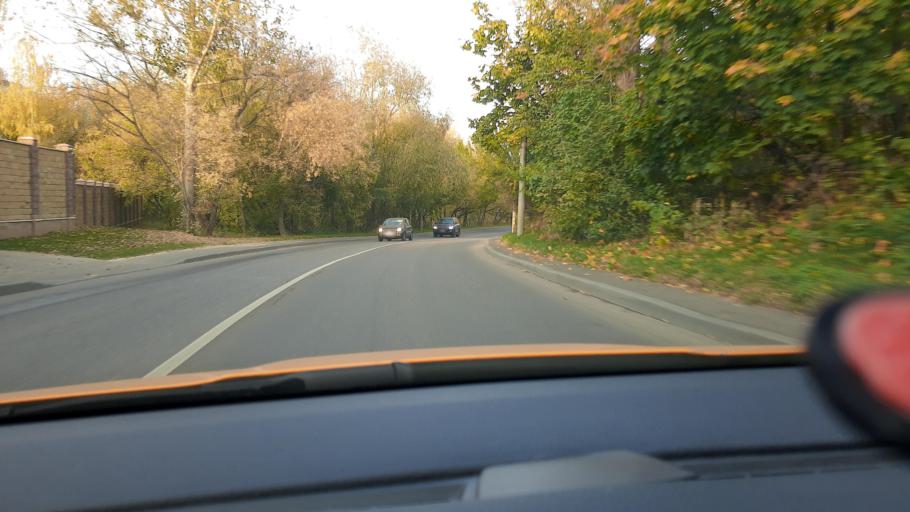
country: RU
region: Moscow
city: Strogino
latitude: 55.7921
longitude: 37.4060
